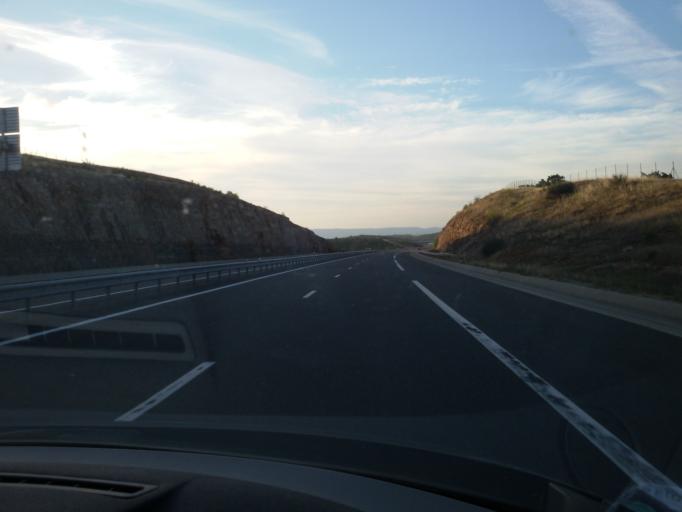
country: FR
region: Midi-Pyrenees
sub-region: Departement de l'Aveyron
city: Creissels
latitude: 44.0358
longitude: 3.0626
